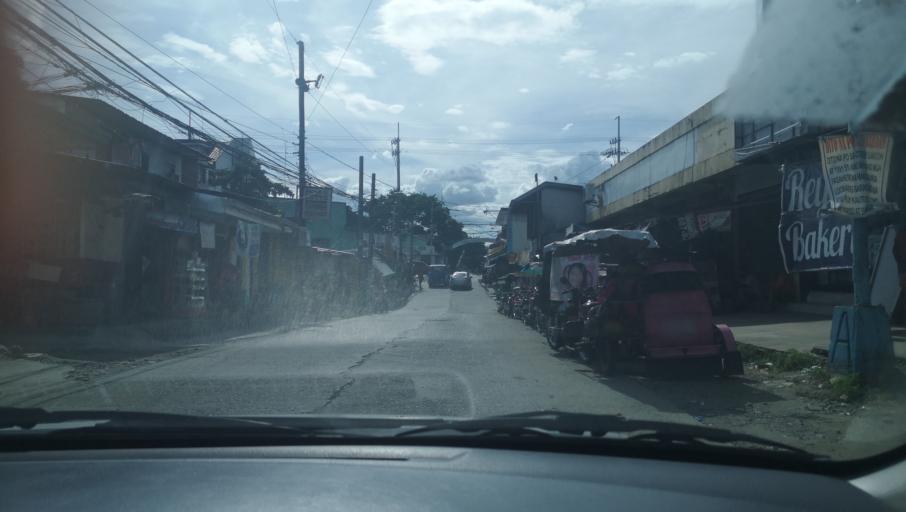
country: PH
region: Calabarzon
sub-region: Province of Rizal
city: San Mateo
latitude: 14.6750
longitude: 121.1106
